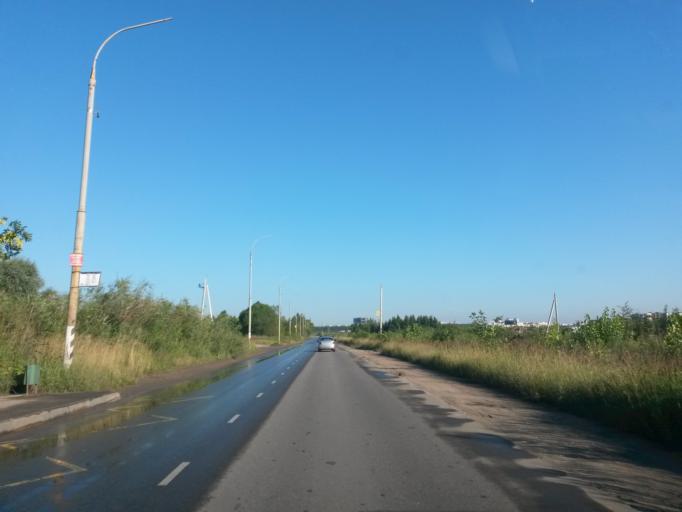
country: RU
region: Moskovskaya
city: Shcherbinka
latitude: 55.5188
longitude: 37.5843
